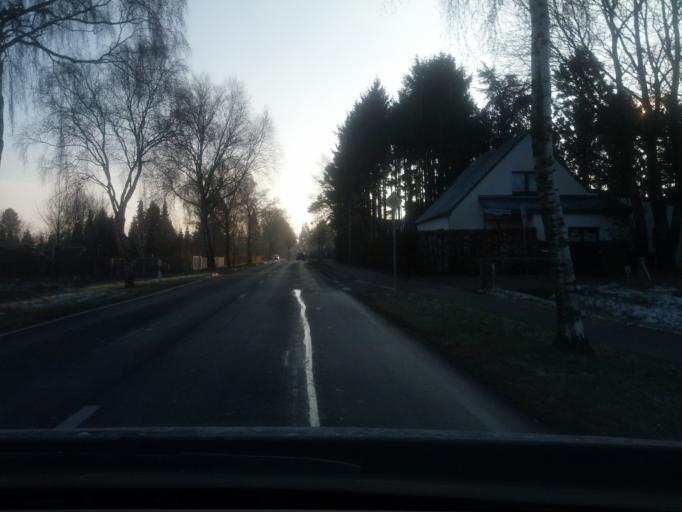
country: DE
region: Lower Saxony
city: Dohren
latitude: 53.2866
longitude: 9.7011
